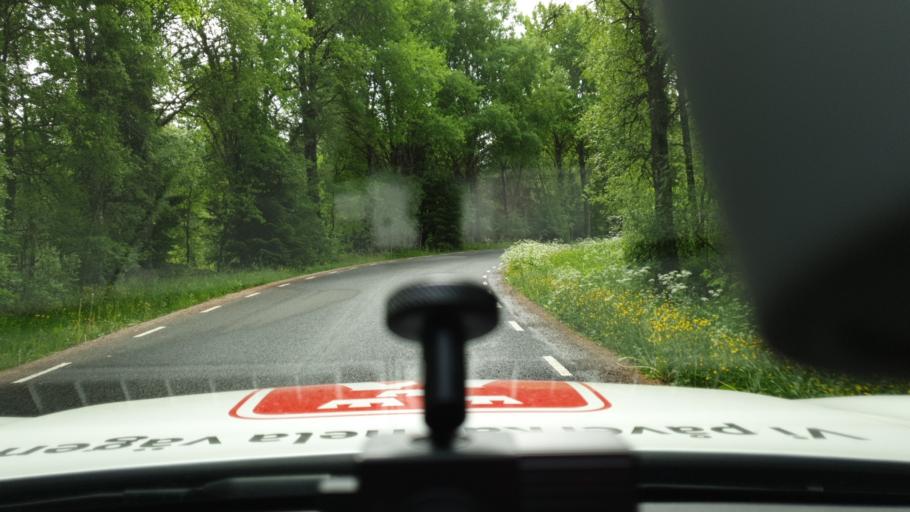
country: SE
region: Joenkoeping
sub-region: Mullsjo Kommun
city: Mullsjoe
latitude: 58.0078
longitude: 13.7180
